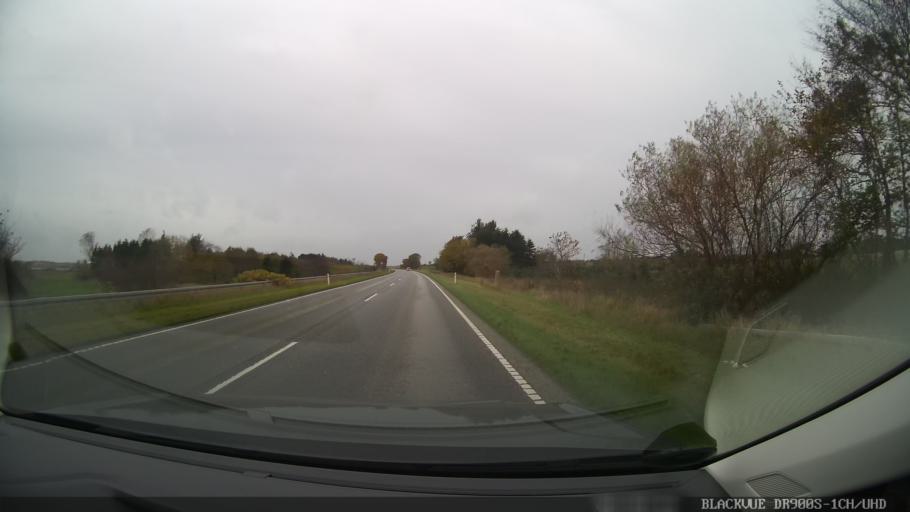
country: DK
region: North Denmark
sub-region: Morso Kommune
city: Nykobing Mors
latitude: 56.8251
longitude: 8.7535
